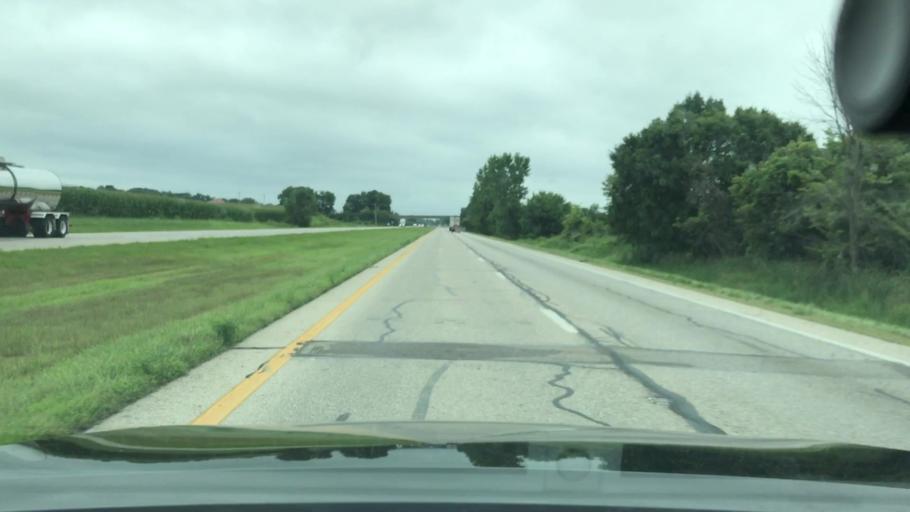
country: US
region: Ohio
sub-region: Ross County
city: Kingston
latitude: 39.4837
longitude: -82.9715
